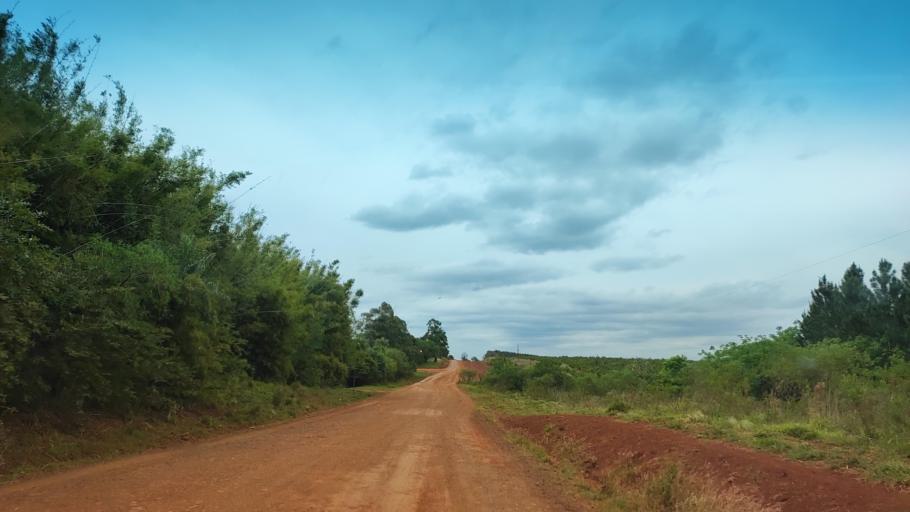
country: AR
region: Misiones
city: Garupa
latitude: -27.4902
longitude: -55.9707
